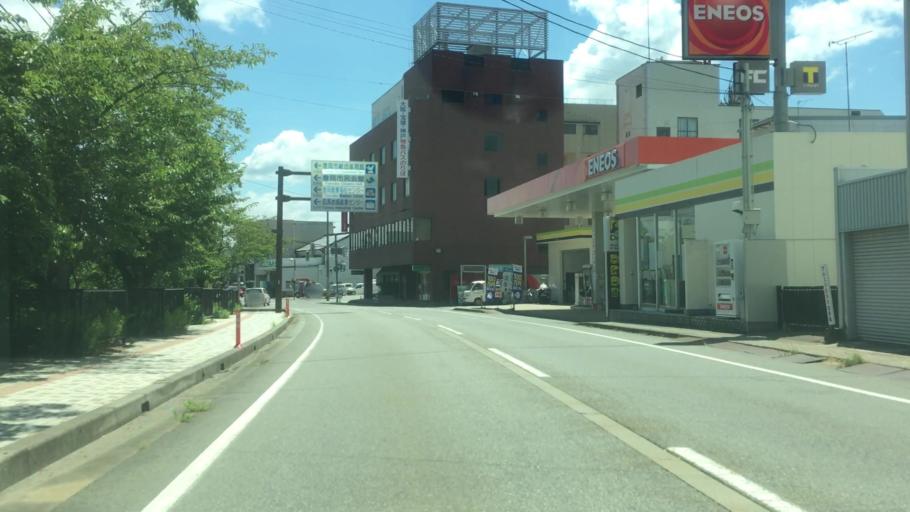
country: JP
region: Hyogo
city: Toyooka
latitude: 35.5410
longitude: 134.8242
